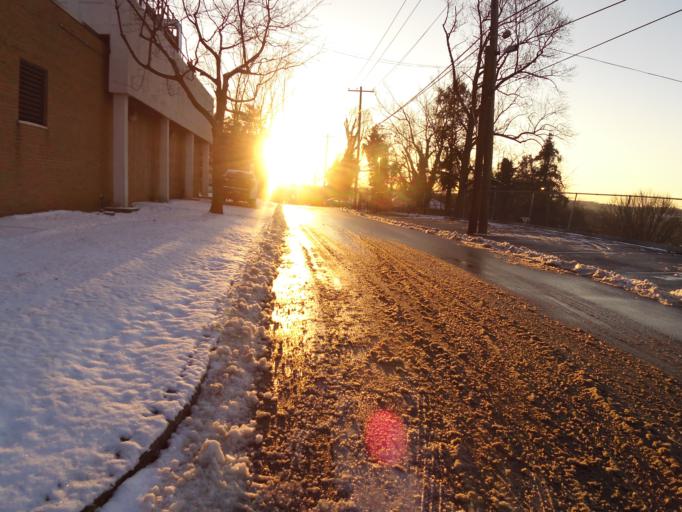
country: US
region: Tennessee
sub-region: Knox County
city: Knoxville
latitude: 35.9532
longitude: -83.9346
